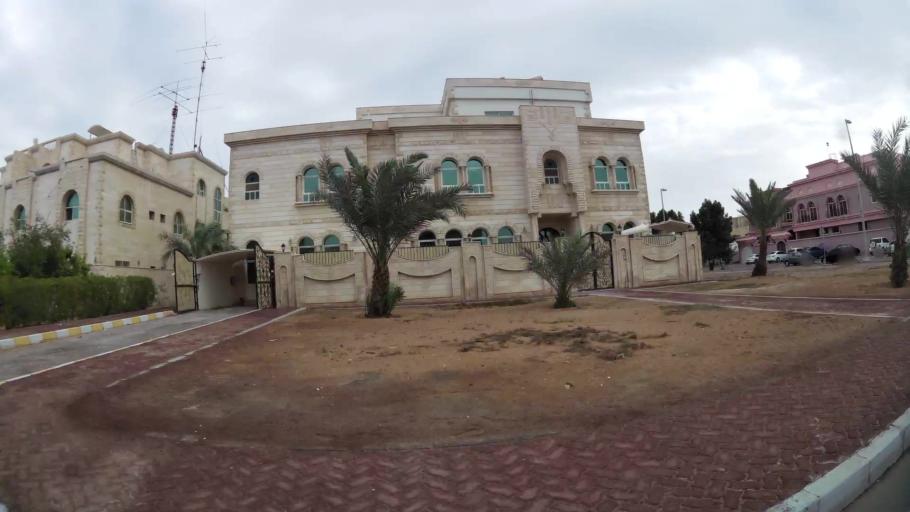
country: AE
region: Abu Dhabi
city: Abu Dhabi
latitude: 24.4324
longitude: 54.4065
